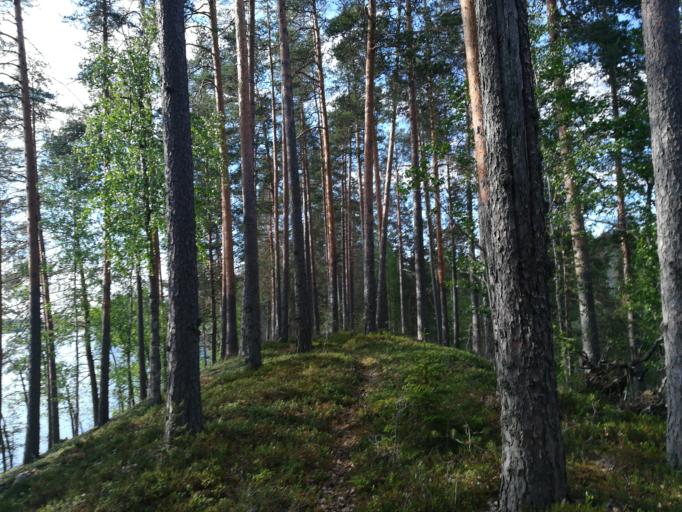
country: FI
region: Southern Savonia
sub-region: Savonlinna
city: Savonlinna
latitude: 61.6413
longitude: 28.7133
